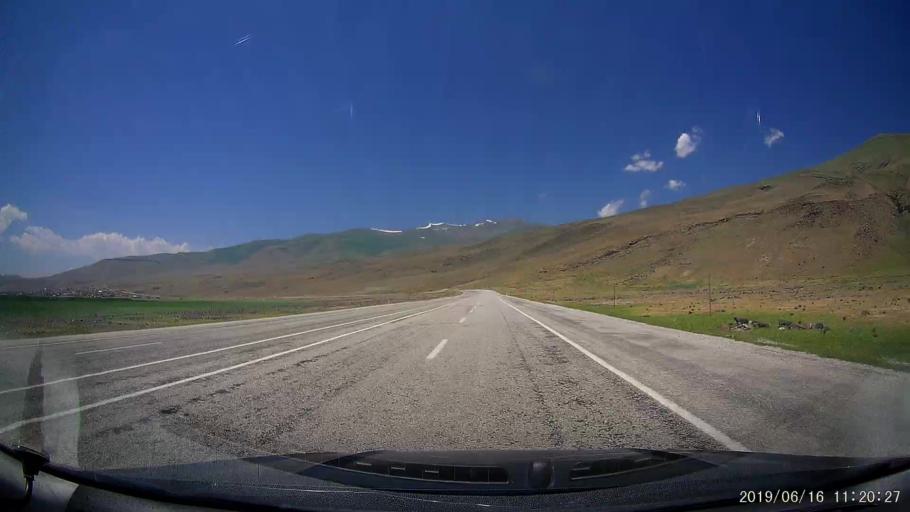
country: TR
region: Agri
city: Dogubayazit
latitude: 39.6989
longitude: 44.0902
